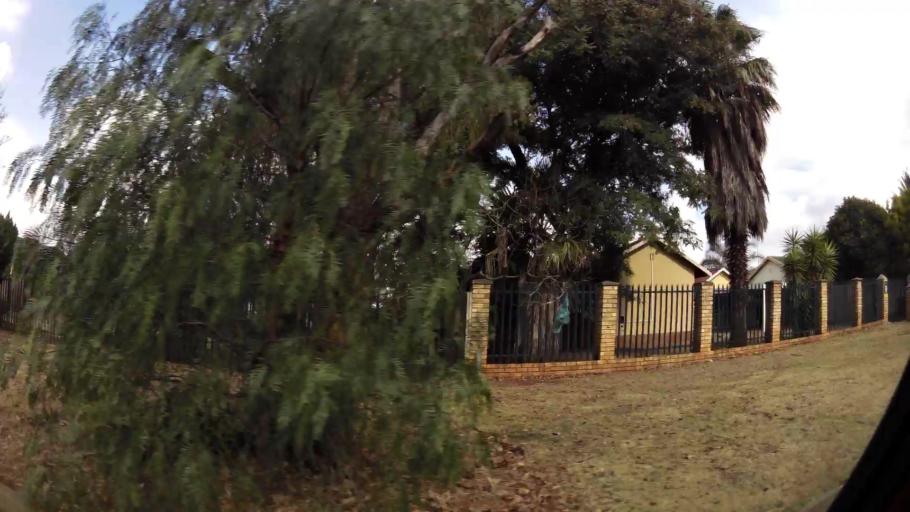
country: ZA
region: Gauteng
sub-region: Sedibeng District Municipality
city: Vanderbijlpark
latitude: -26.7178
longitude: 27.8602
